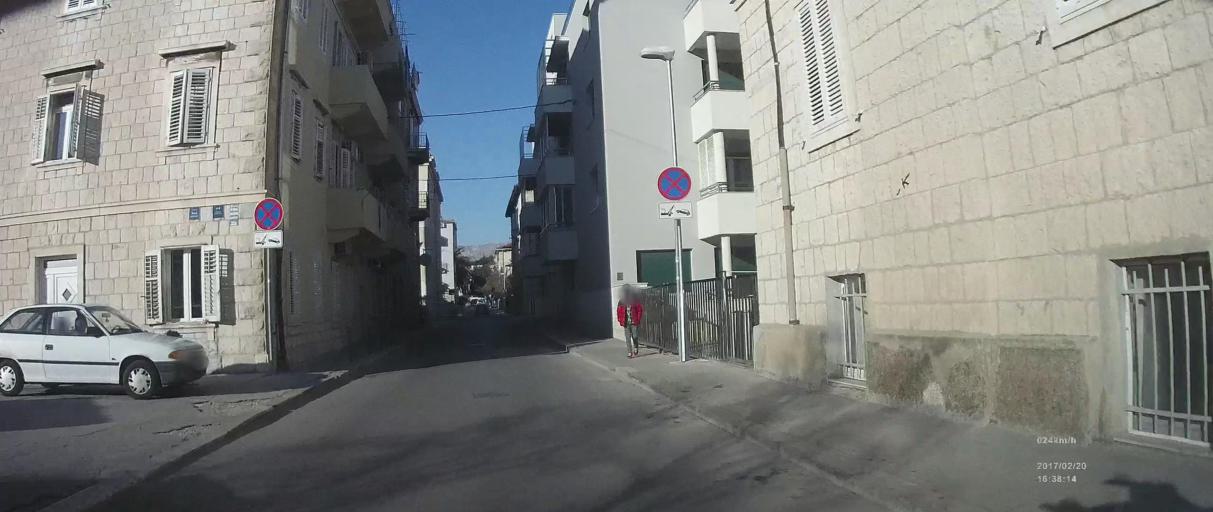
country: HR
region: Splitsko-Dalmatinska
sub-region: Grad Split
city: Split
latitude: 43.5019
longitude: 16.4450
